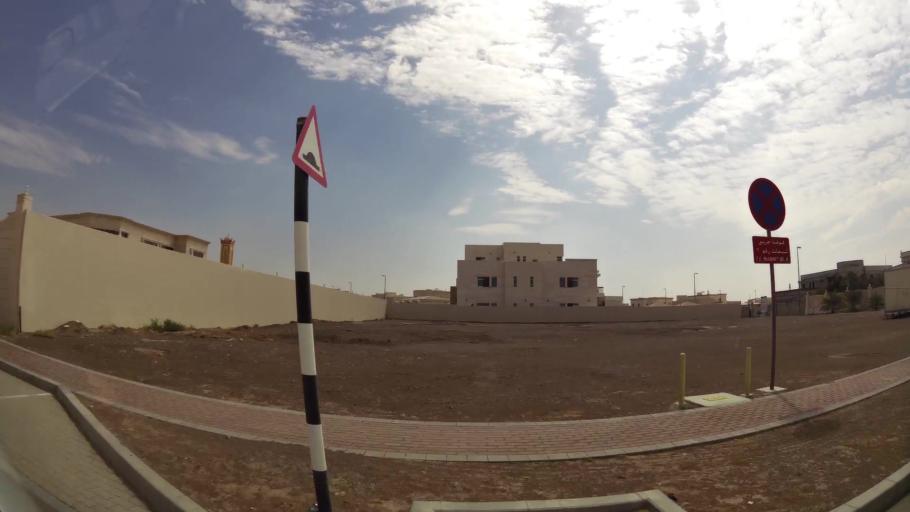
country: AE
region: Abu Dhabi
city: Al Ain
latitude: 24.1978
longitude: 55.8072
